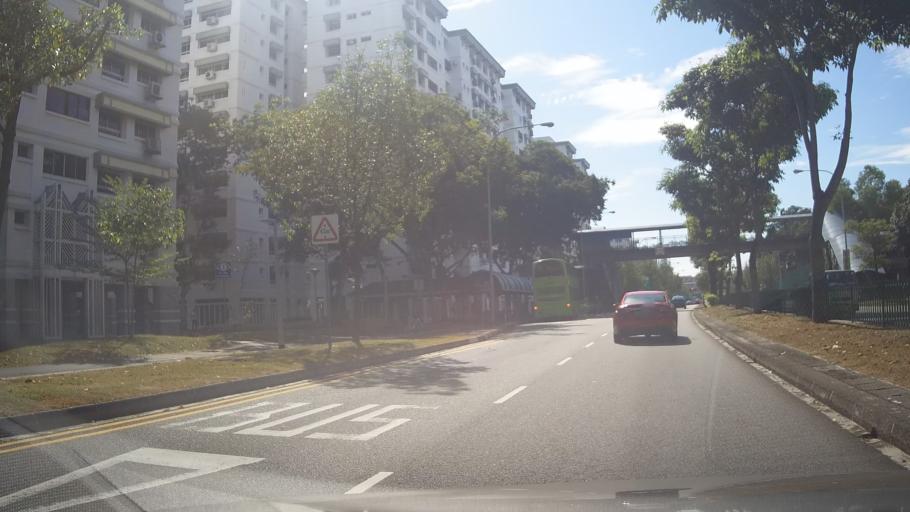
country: MY
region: Johor
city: Kampung Pasir Gudang Baru
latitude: 1.3671
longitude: 103.9605
